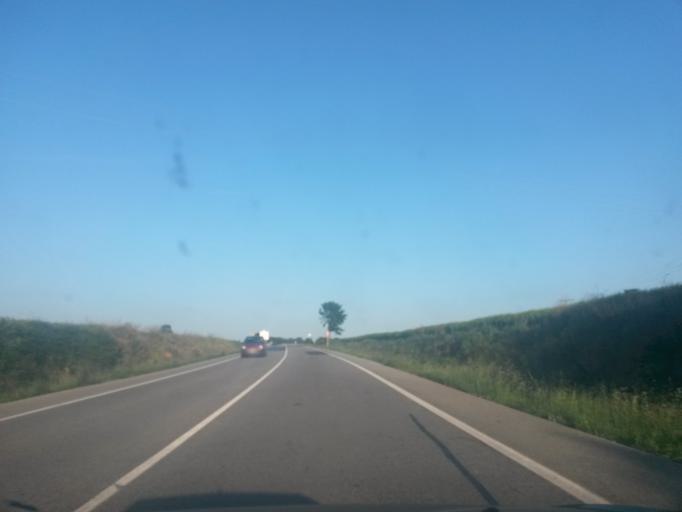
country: ES
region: Catalonia
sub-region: Provincia de Girona
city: Porqueres
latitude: 42.1540
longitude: 2.7520
